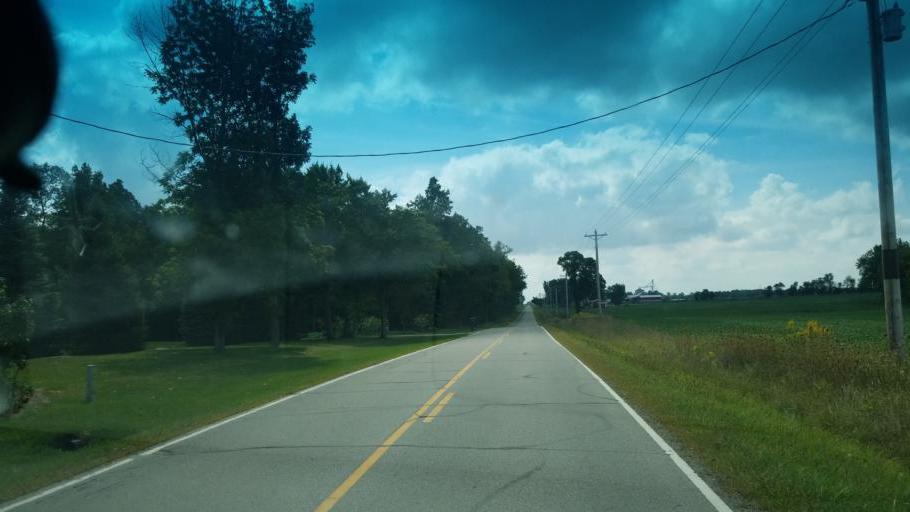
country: US
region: Ohio
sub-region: Crawford County
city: Bucyrus
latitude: 40.9638
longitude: -82.9016
